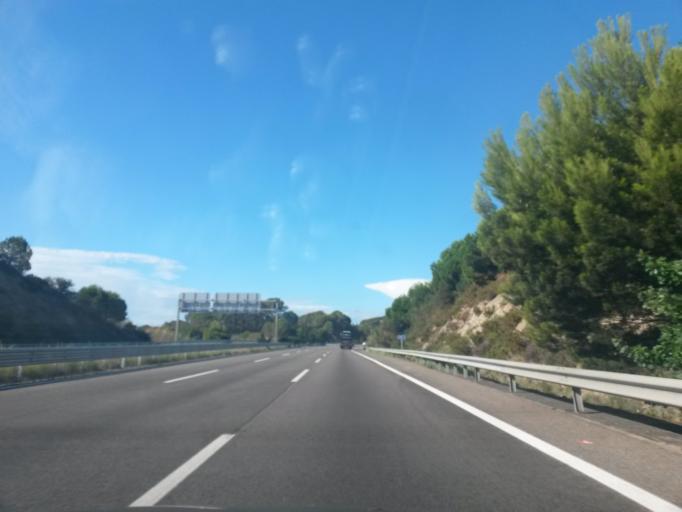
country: ES
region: Catalonia
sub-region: Provincia de Barcelona
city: Calella
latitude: 41.6232
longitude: 2.6481
